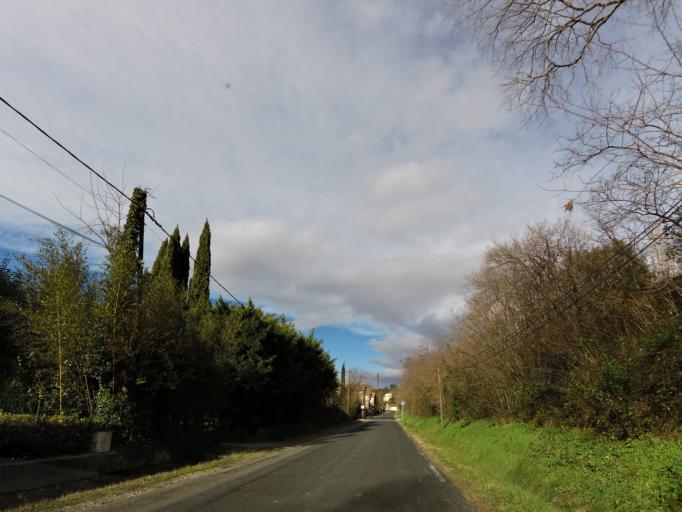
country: FR
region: Languedoc-Roussillon
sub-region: Departement du Gard
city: Sommieres
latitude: 43.7742
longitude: 4.0925
